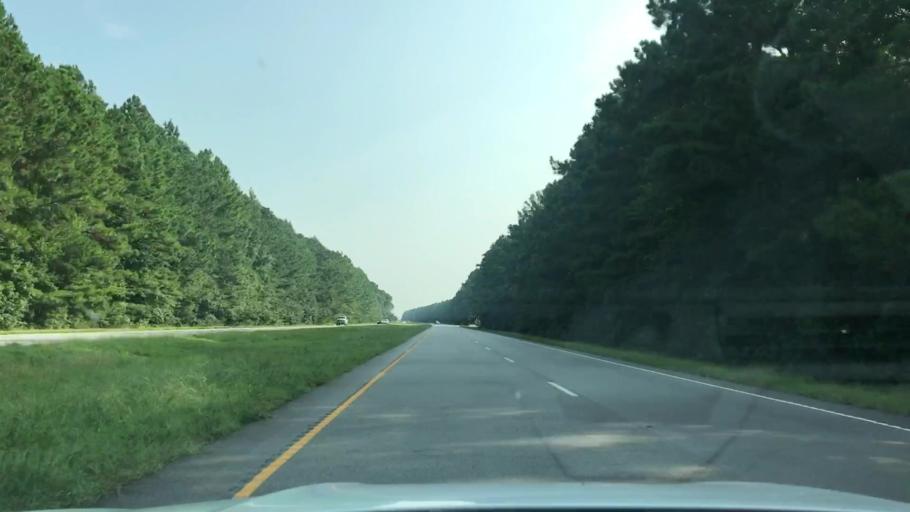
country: US
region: South Carolina
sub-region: Charleston County
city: Awendaw
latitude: 33.1182
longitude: -79.4547
